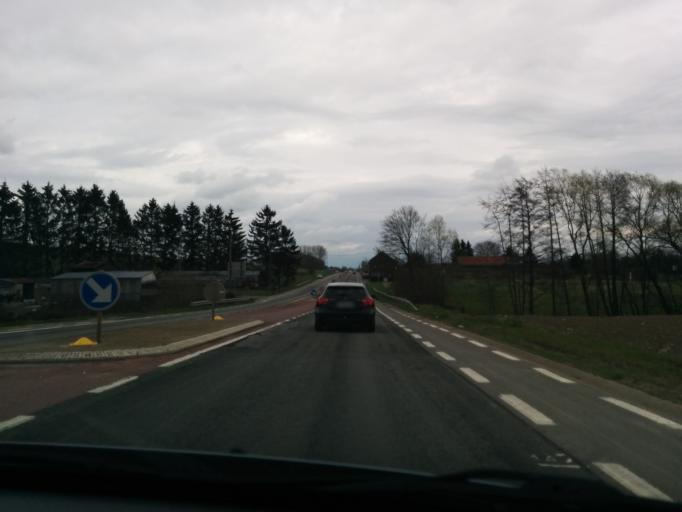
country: BE
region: Wallonia
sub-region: Province de Namur
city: Fosses-la-Ville
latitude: 50.3954
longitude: 4.7139
